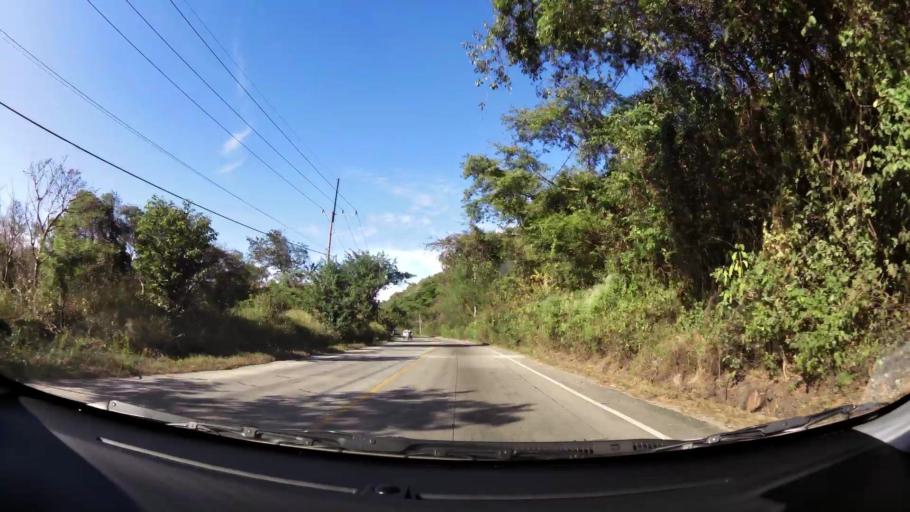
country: SV
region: Santa Ana
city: Metapan
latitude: 14.2622
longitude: -89.4598
